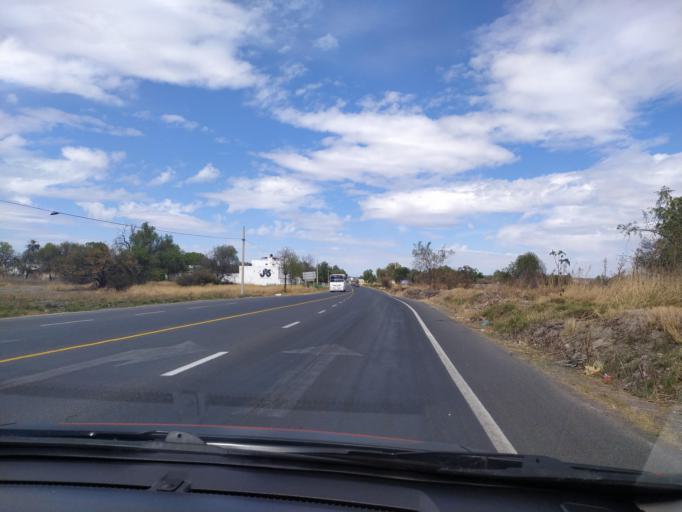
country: LA
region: Oudomxai
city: Muang La
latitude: 21.0120
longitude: 101.8284
